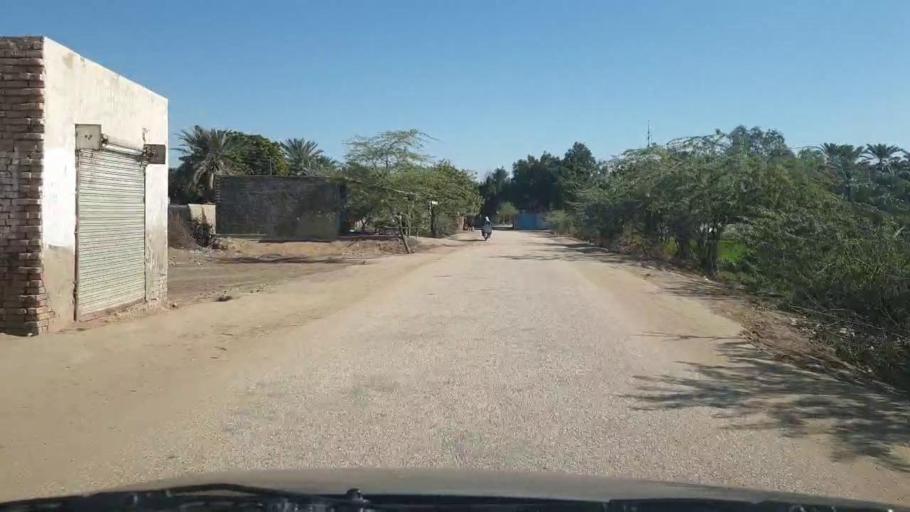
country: PK
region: Sindh
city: Bozdar
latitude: 27.0591
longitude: 68.6423
